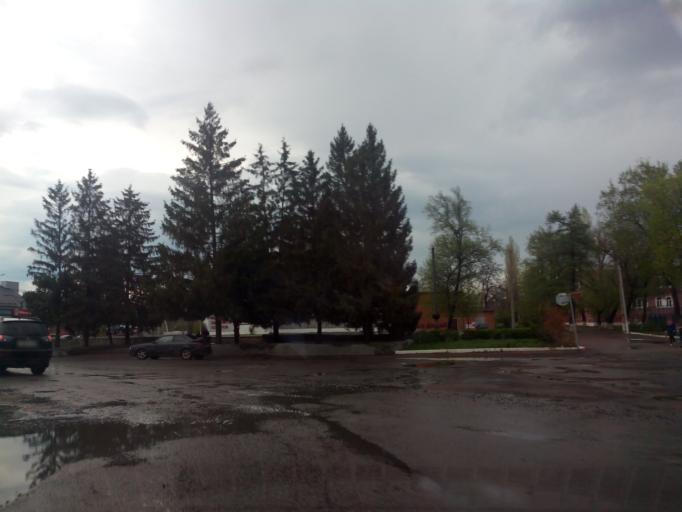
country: RU
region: Voronezj
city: Borisoglebsk
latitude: 51.3706
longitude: 42.0752
